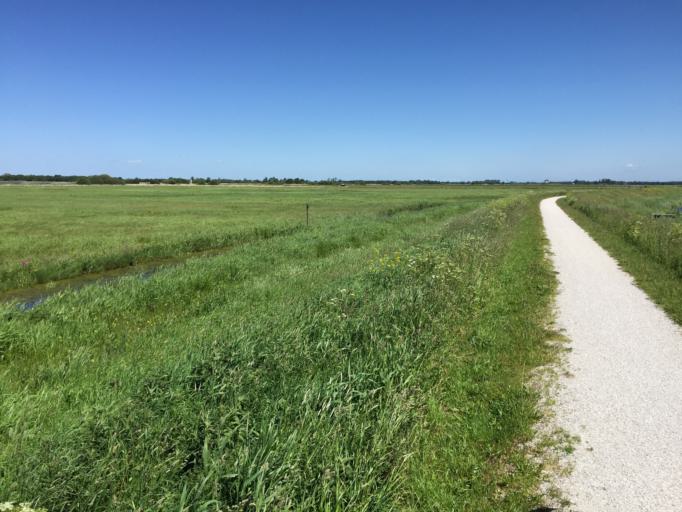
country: NL
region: Friesland
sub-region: Gemeente Smallingerland
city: Oudega
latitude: 53.1027
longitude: 5.9713
